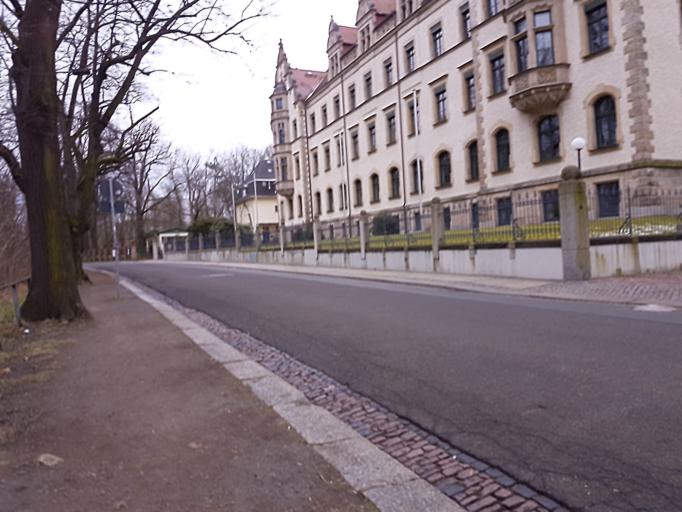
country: DE
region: Saxony
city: Chemnitz
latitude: 50.8357
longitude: 12.9118
